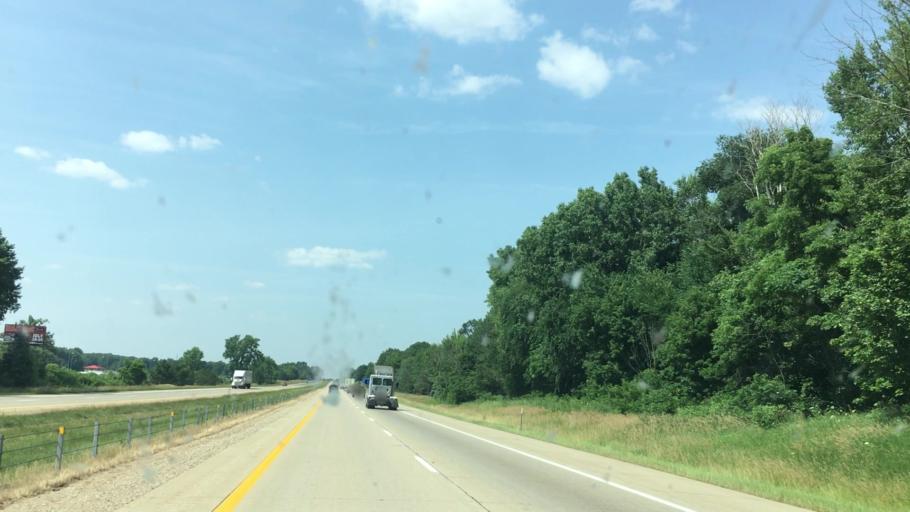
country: US
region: Michigan
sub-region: Allegan County
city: Otsego
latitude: 42.5116
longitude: -85.6550
